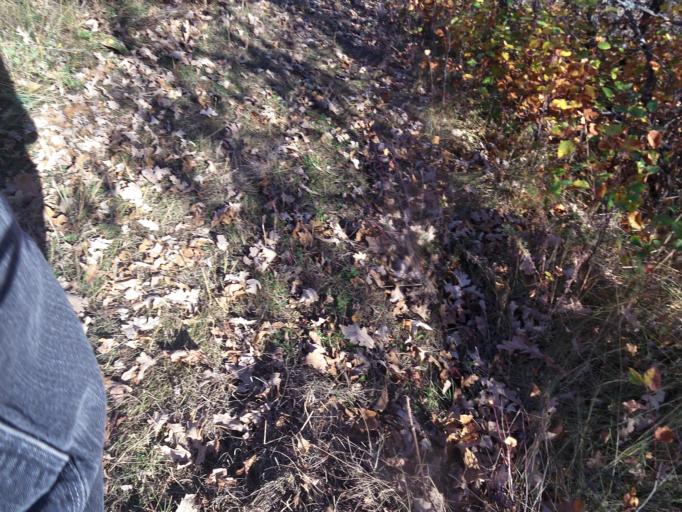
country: CA
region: Manitoba
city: Morden
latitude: 48.9469
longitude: -98.0738
